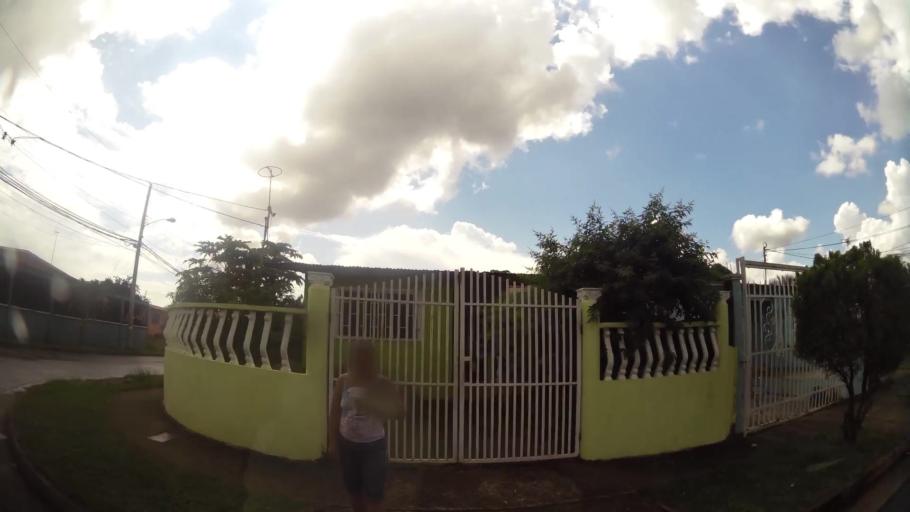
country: PA
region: Panama
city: Nuevo Arraijan
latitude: 8.9368
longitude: -79.7379
